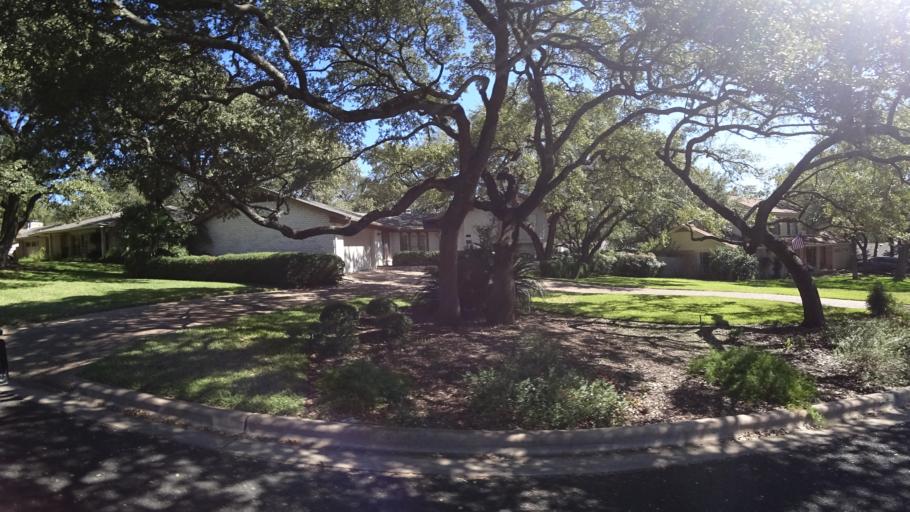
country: US
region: Texas
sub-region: Williamson County
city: Jollyville
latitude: 30.3656
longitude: -97.7604
